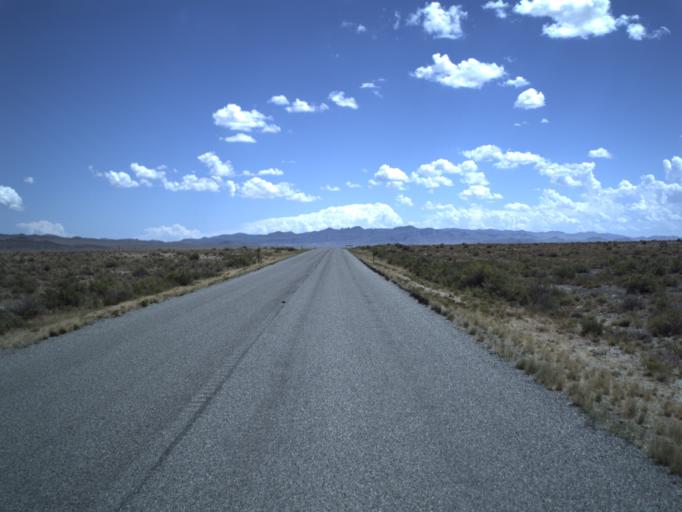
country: US
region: Nevada
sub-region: White Pine County
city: McGill
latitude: 39.0511
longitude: -113.9701
